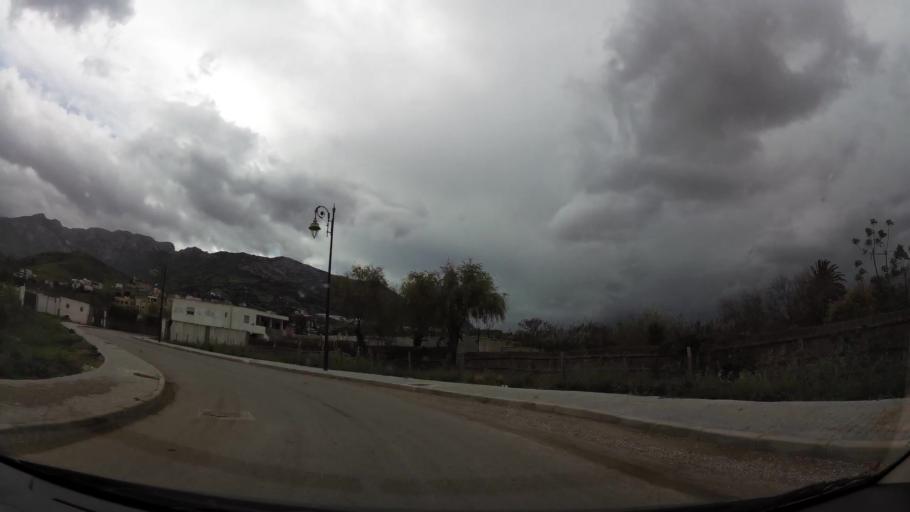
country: MA
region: Tanger-Tetouan
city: Tetouan
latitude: 35.5559
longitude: -5.3534
